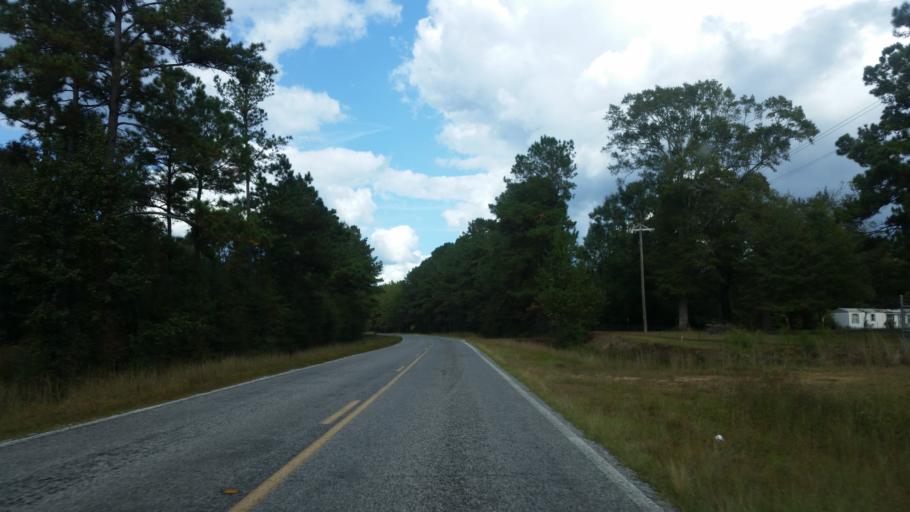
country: US
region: Mississippi
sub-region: Stone County
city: Wiggins
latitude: 30.9395
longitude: -89.0522
